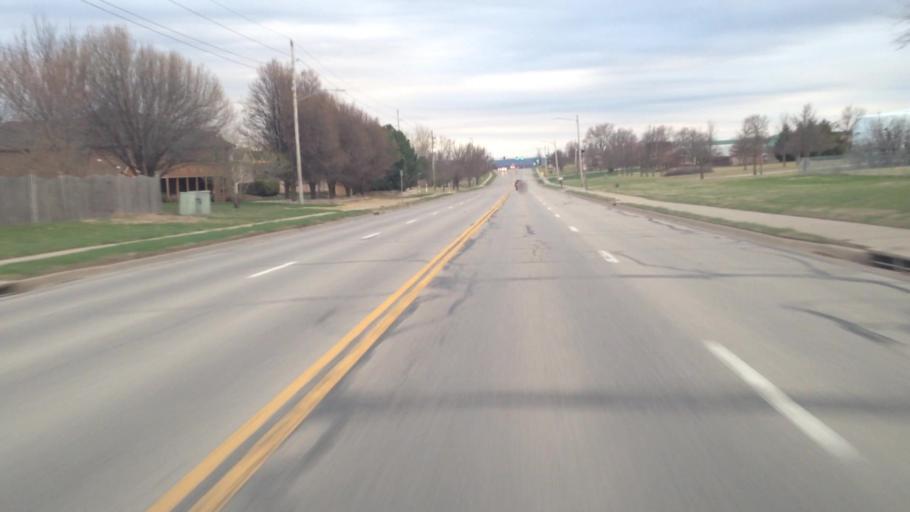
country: US
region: Kansas
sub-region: Douglas County
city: Lawrence
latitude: 38.9476
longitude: -95.3072
